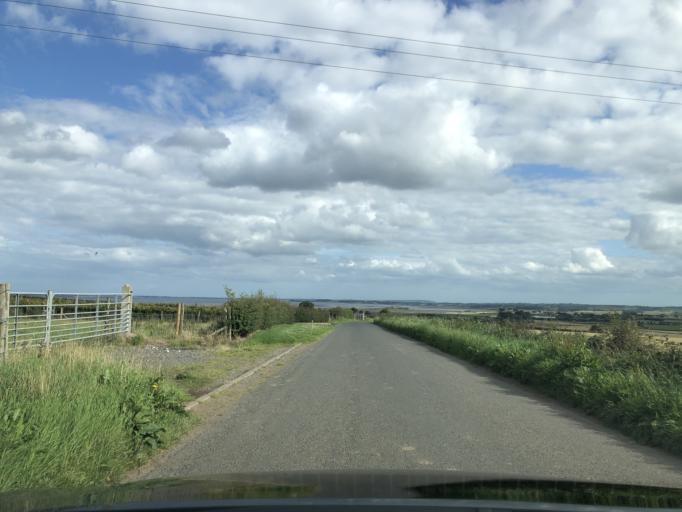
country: GB
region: Northern Ireland
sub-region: Ards District
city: Newtownards
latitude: 54.5723
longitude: -5.7150
